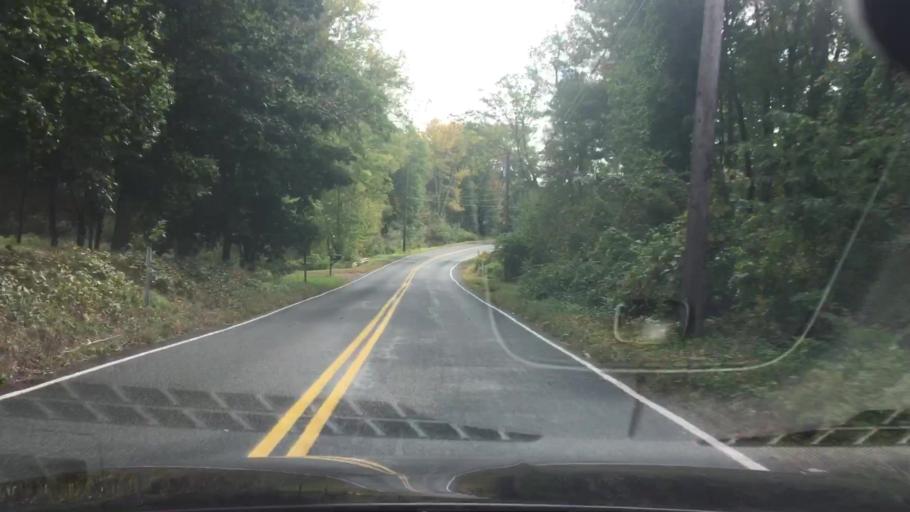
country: US
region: Connecticut
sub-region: Tolland County
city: Somers
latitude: 41.9928
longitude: -72.4946
